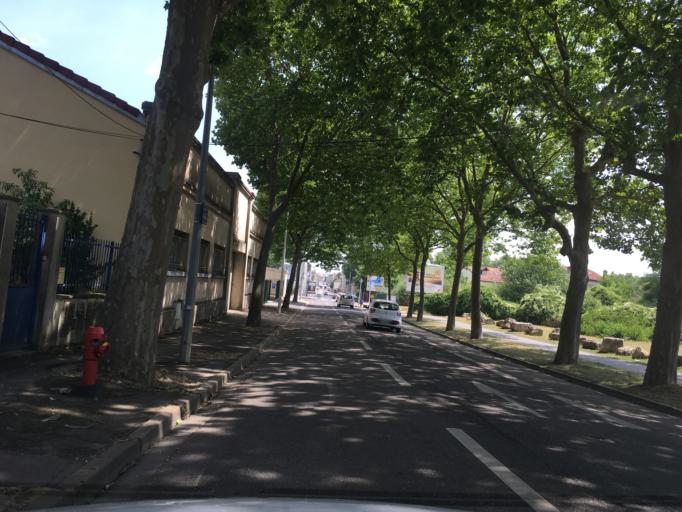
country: FR
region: Lorraine
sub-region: Departement de Meurthe-et-Moselle
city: Nancy
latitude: 48.6861
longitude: 6.1978
